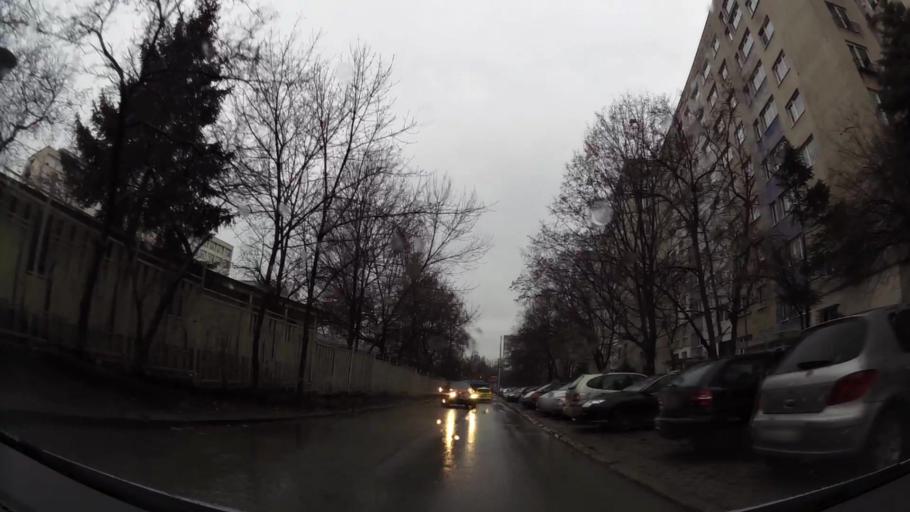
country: BG
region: Sofia-Capital
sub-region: Stolichna Obshtina
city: Sofia
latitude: 42.6593
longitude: 23.3735
